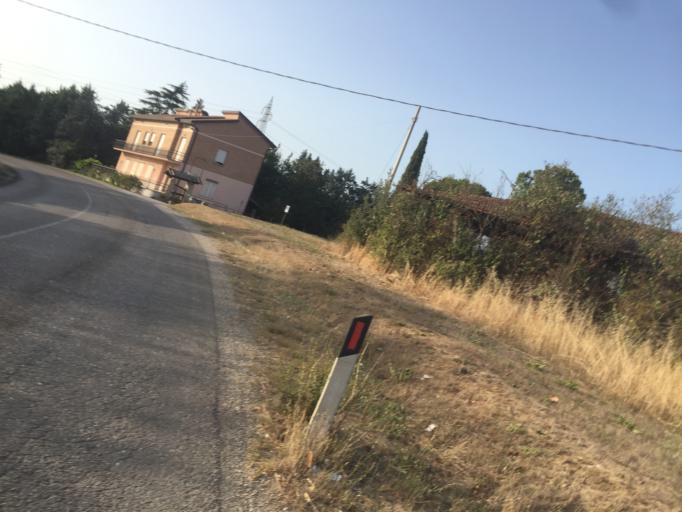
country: IT
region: Umbria
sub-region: Provincia di Perugia
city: Torgiano
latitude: 43.0325
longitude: 12.4270
